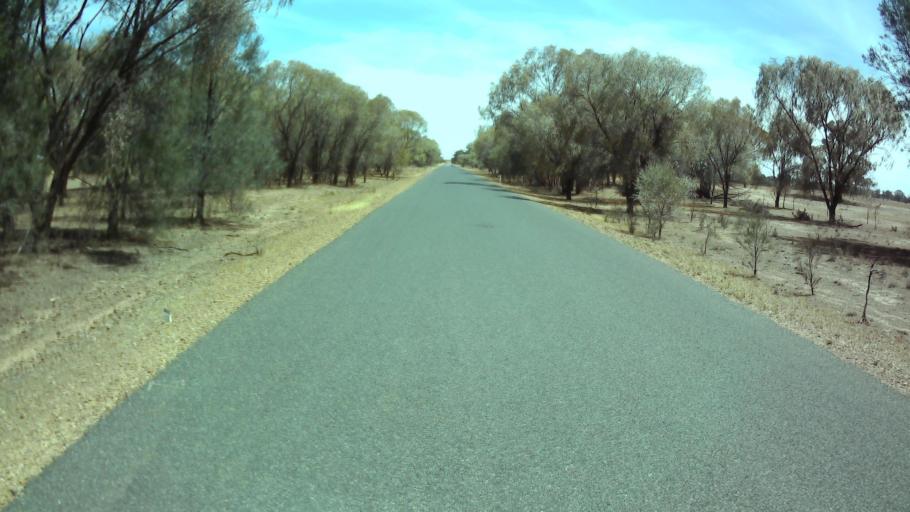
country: AU
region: New South Wales
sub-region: Weddin
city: Grenfell
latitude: -33.8745
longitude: 147.7440
